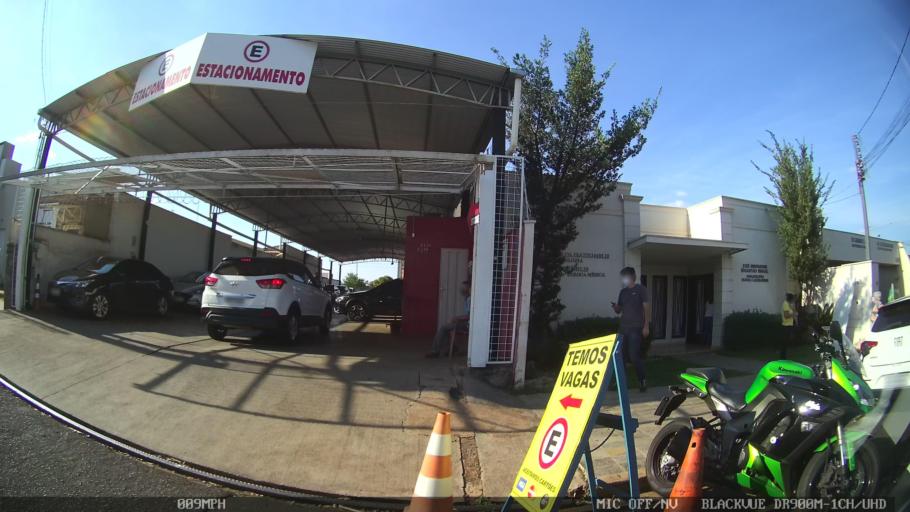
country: BR
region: Sao Paulo
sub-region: Ribeirao Preto
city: Ribeirao Preto
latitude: -21.1877
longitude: -47.8052
